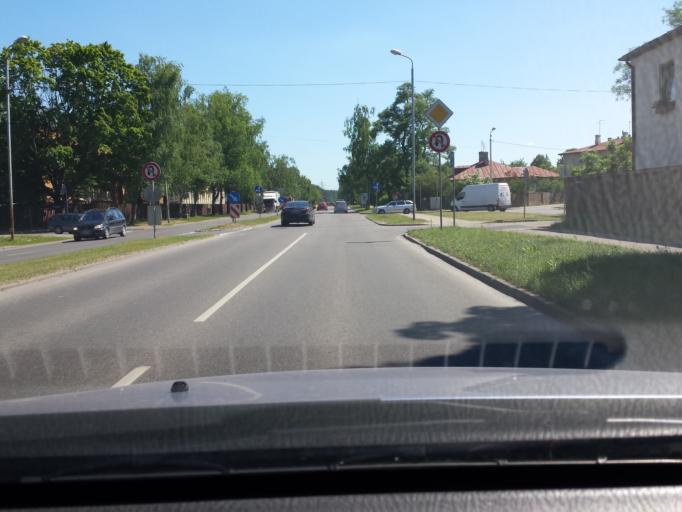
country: LV
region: Riga
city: Jaunciems
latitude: 56.9743
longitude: 24.1898
